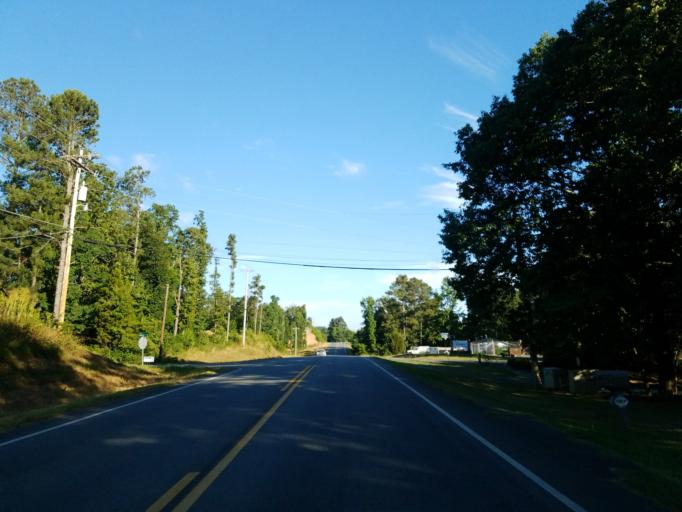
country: US
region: Georgia
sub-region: Gordon County
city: Calhoun
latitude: 34.5223
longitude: -84.9691
